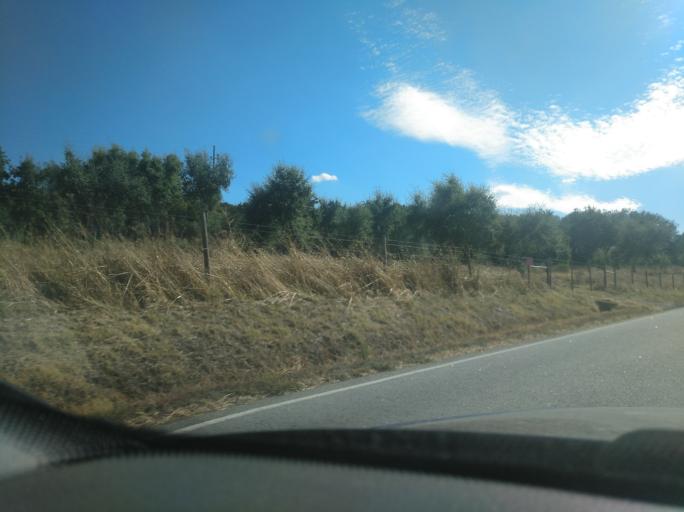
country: PT
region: Portalegre
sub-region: Arronches
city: Arronches
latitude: 39.1452
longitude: -7.2234
